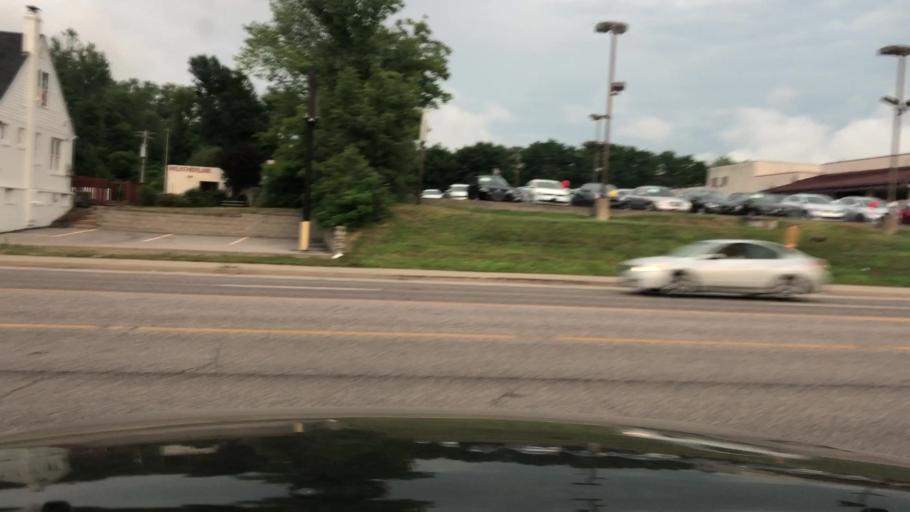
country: US
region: Missouri
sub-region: Saint Louis County
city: Bridgeton
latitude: 38.7497
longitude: -90.4249
